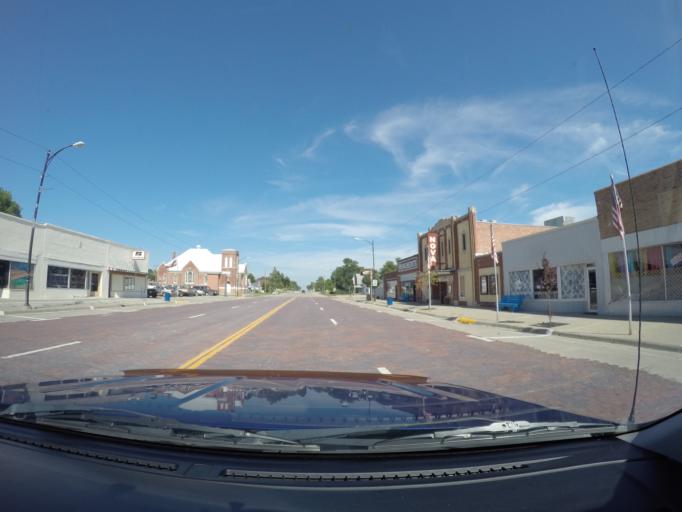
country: US
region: Kansas
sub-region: Rooks County
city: Stockton
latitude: 39.4367
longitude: -99.2731
